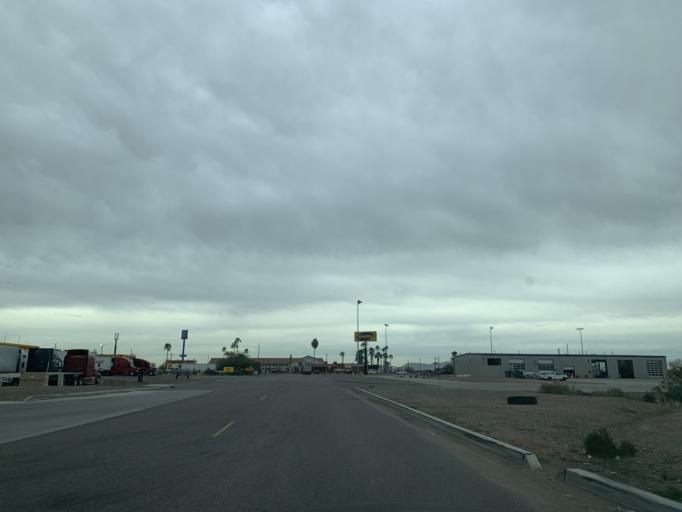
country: US
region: Arizona
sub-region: Pinal County
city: Arizona City
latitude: 32.8059
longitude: -111.6735
